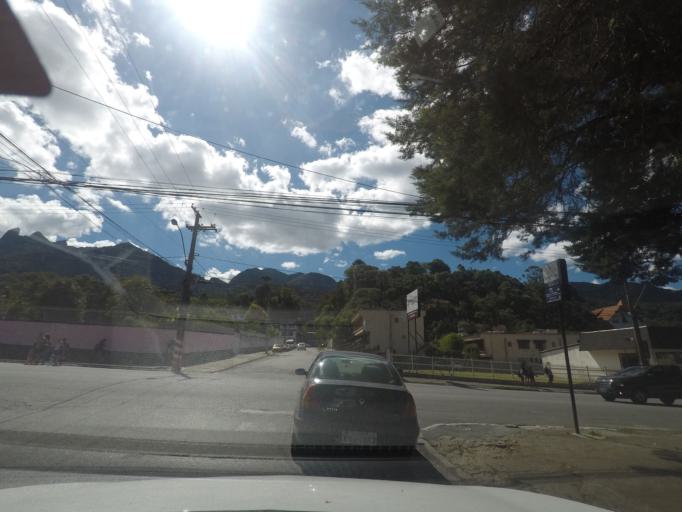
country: BR
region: Rio de Janeiro
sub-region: Teresopolis
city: Teresopolis
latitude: -22.4444
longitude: -42.9812
